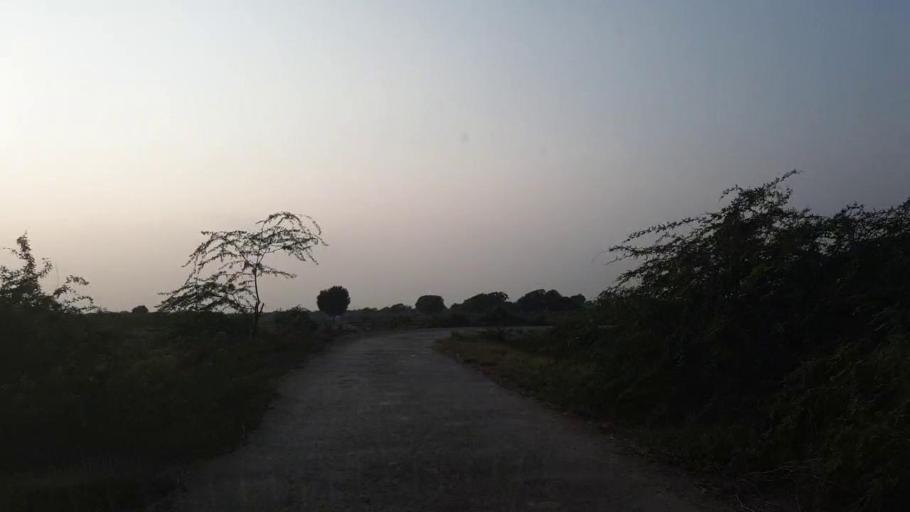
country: PK
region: Sindh
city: Tando Ghulam Ali
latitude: 25.0786
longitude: 68.9590
